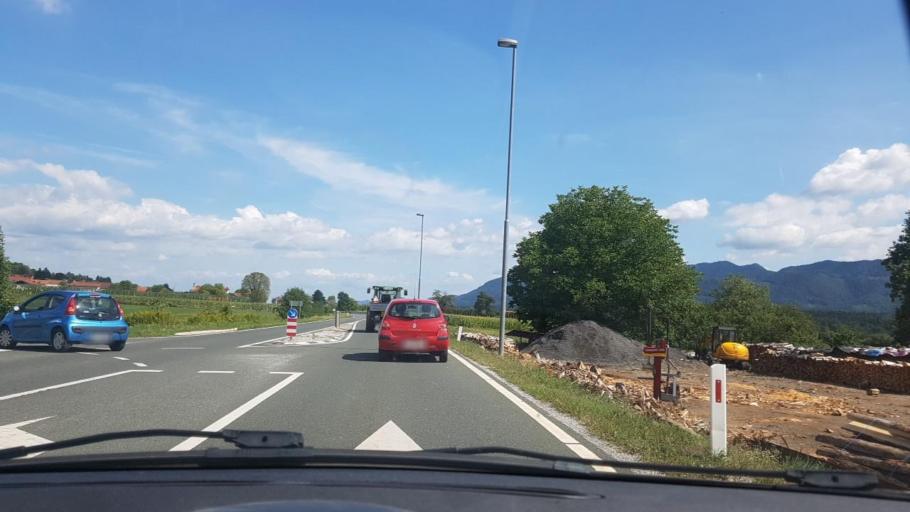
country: SI
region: Vransko
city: Vransko
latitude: 46.2491
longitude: 14.9809
